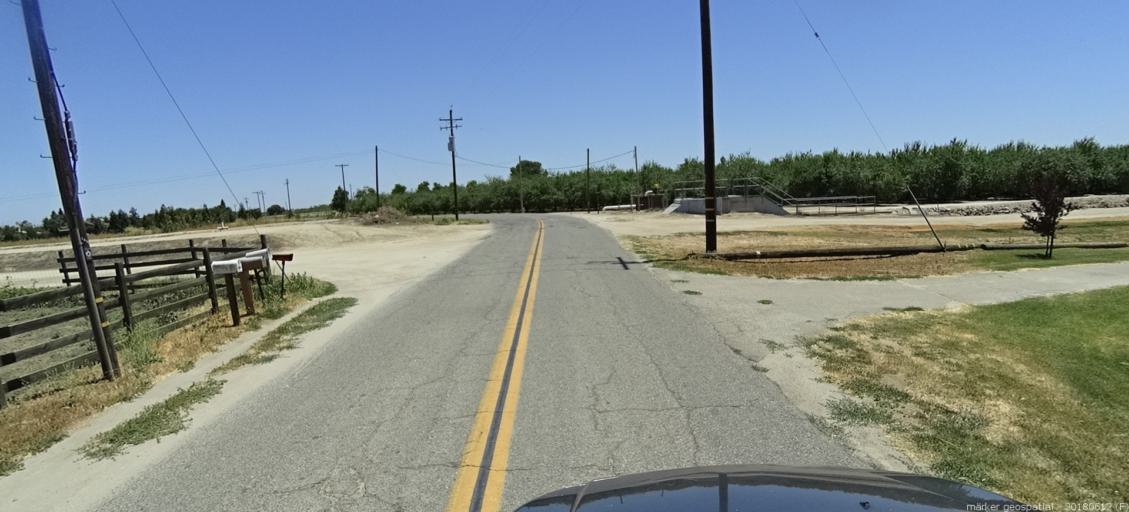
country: US
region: California
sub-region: Madera County
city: Chowchilla
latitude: 37.0910
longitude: -120.2858
